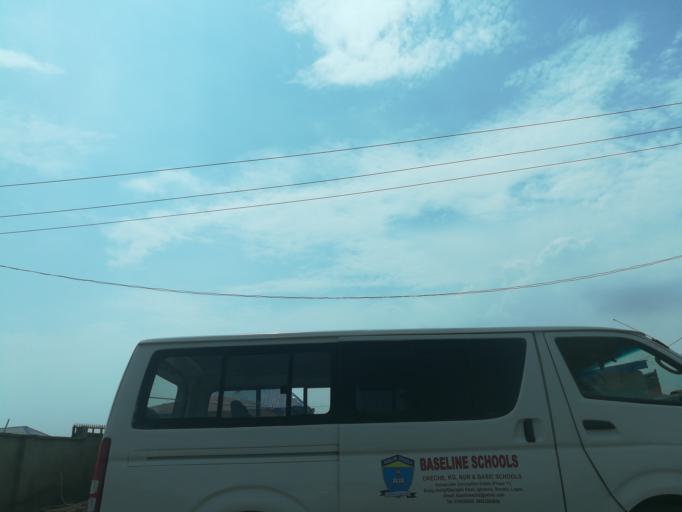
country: NG
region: Lagos
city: Ikorodu
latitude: 6.5979
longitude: 3.6248
